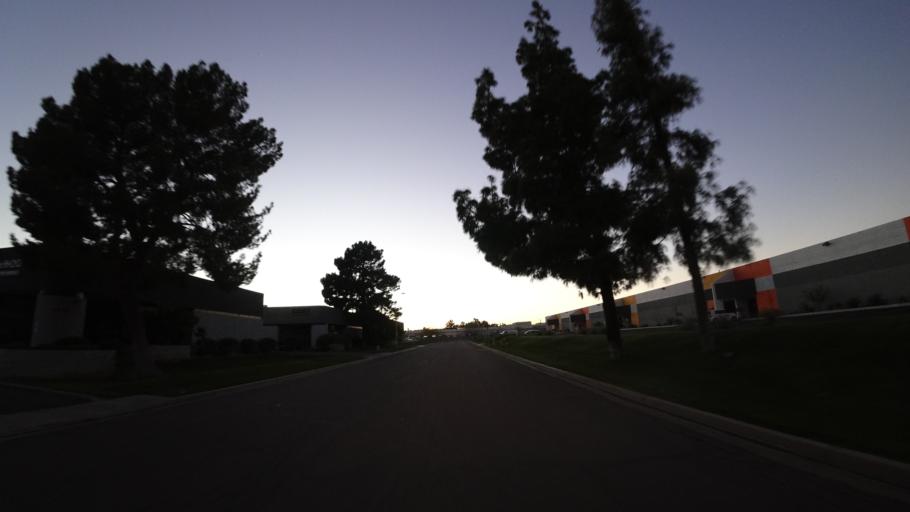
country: US
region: Arizona
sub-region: Maricopa County
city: Tempe Junction
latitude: 33.4156
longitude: -111.9653
